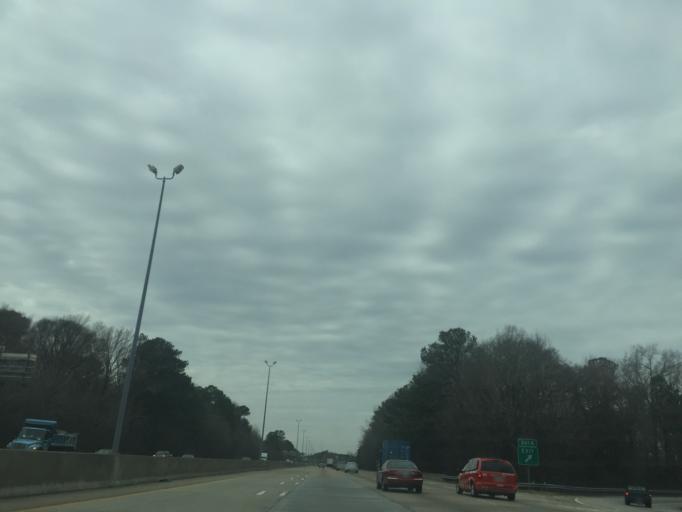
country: US
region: Virginia
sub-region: City of Hampton
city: Hampton
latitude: 37.0594
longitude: -76.4176
